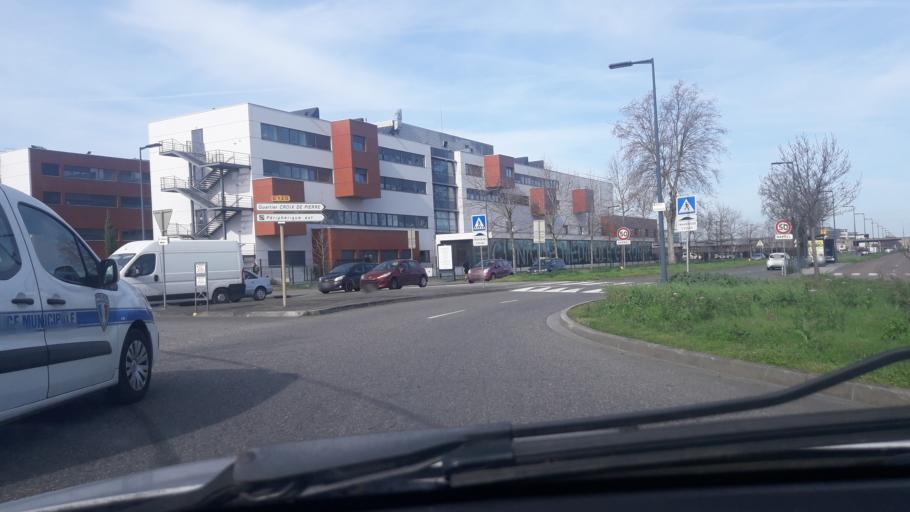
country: FR
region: Midi-Pyrenees
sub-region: Departement de la Haute-Garonne
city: Vieille-Toulouse
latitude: 43.5631
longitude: 1.4254
